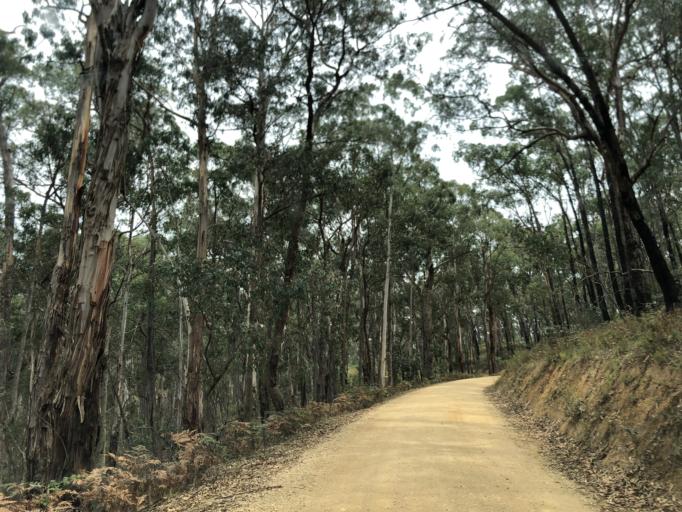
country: AU
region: Victoria
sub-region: Moorabool
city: Bacchus Marsh
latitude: -37.4992
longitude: 144.3503
